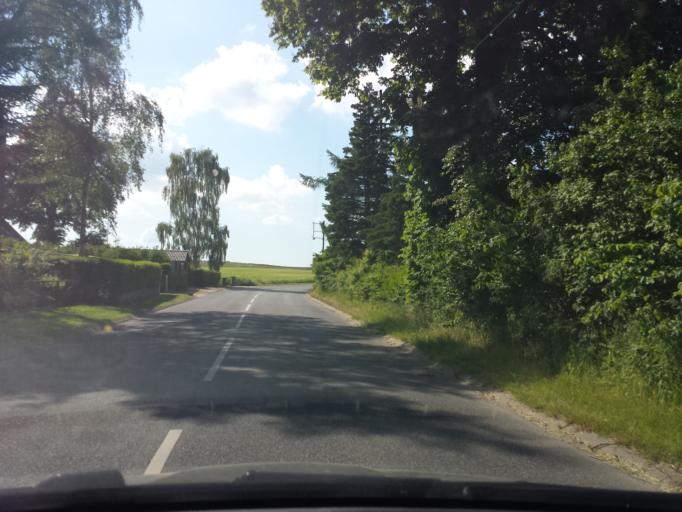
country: DK
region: Capital Region
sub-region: Ballerup Kommune
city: Ballerup
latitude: 55.7025
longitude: 12.3769
